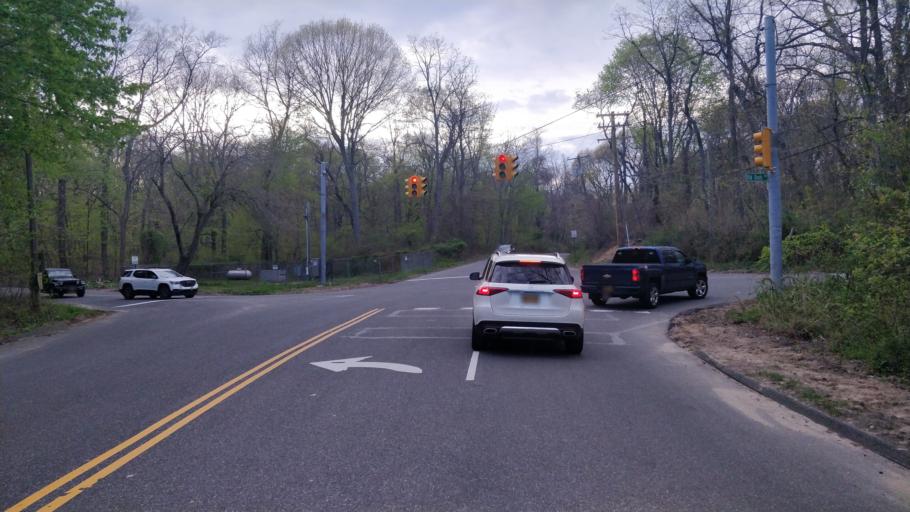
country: US
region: New York
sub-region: Suffolk County
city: Kings Park
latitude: 40.9001
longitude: -73.2371
